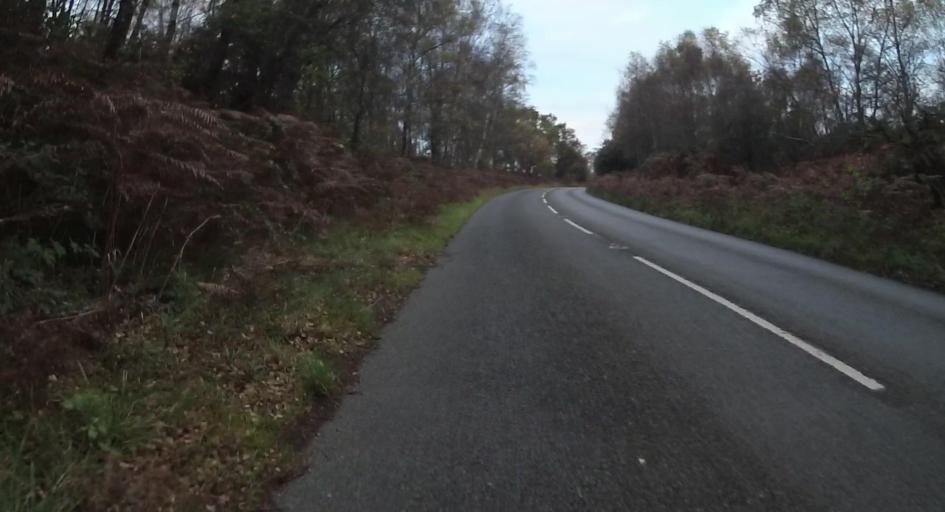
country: GB
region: England
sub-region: Hampshire
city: Lindford
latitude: 51.1285
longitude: -0.8523
